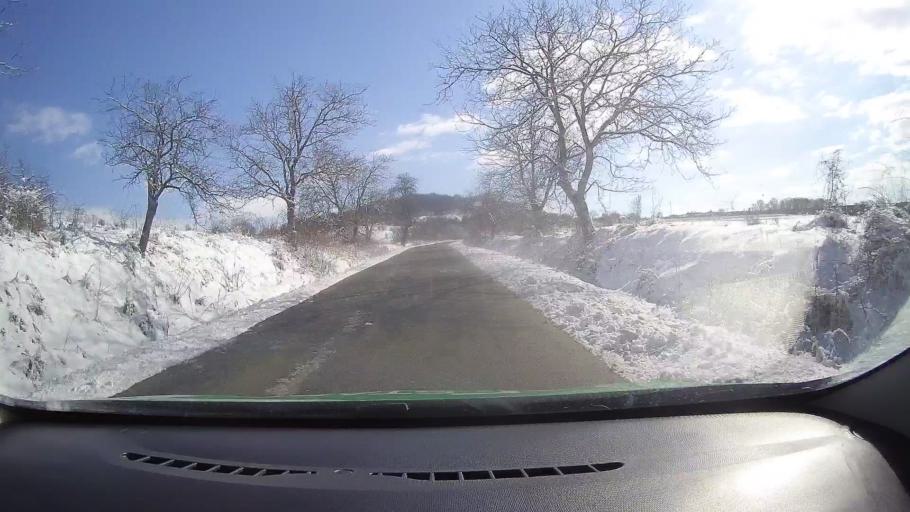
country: RO
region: Sibiu
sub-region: Comuna Mosna
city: Mosna
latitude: 46.0097
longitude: 24.4242
